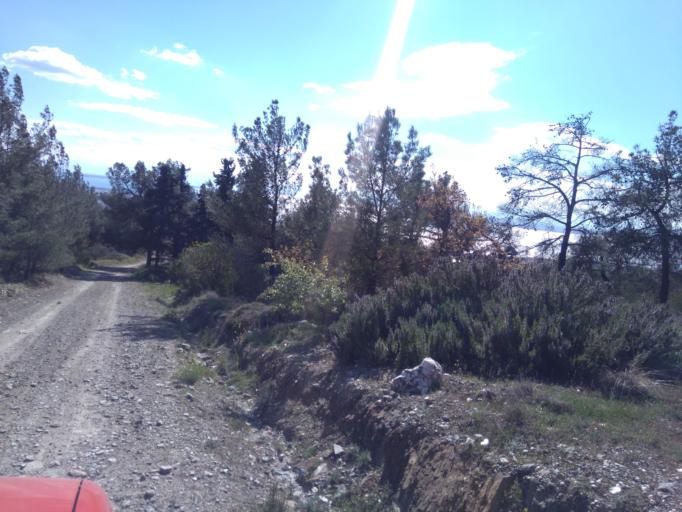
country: GR
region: Central Macedonia
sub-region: Nomos Thessalonikis
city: Triandria
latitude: 40.6338
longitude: 22.9800
